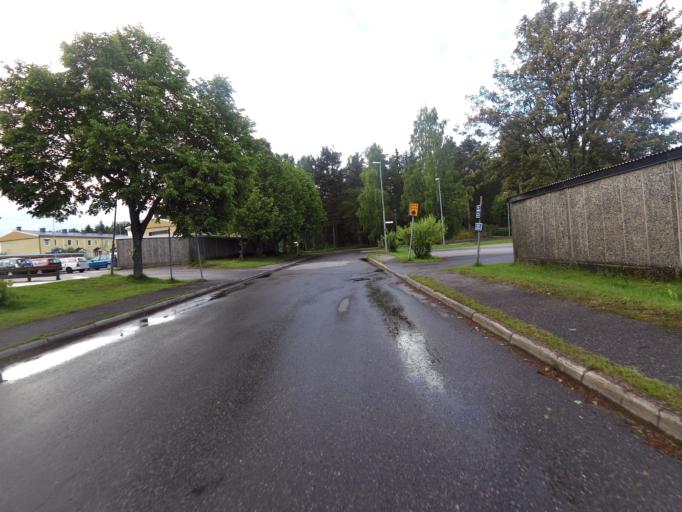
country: SE
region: Gaevleborg
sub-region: Gavle Kommun
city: Gavle
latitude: 60.6935
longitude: 17.1048
